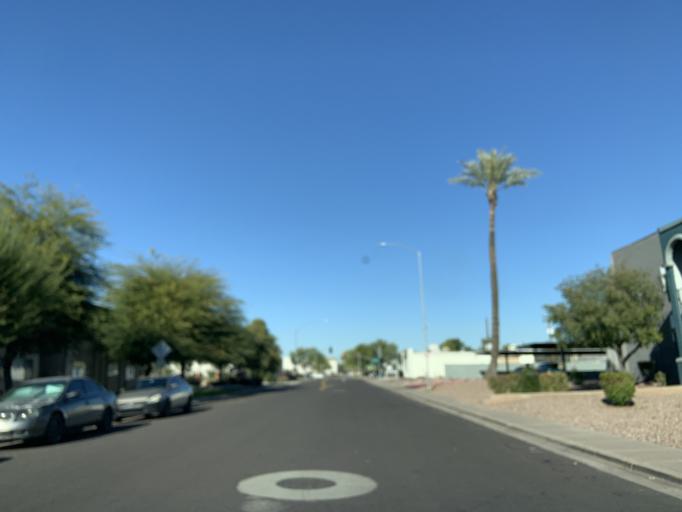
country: US
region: Arizona
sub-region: Maricopa County
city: Tempe
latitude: 33.4063
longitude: -111.8810
